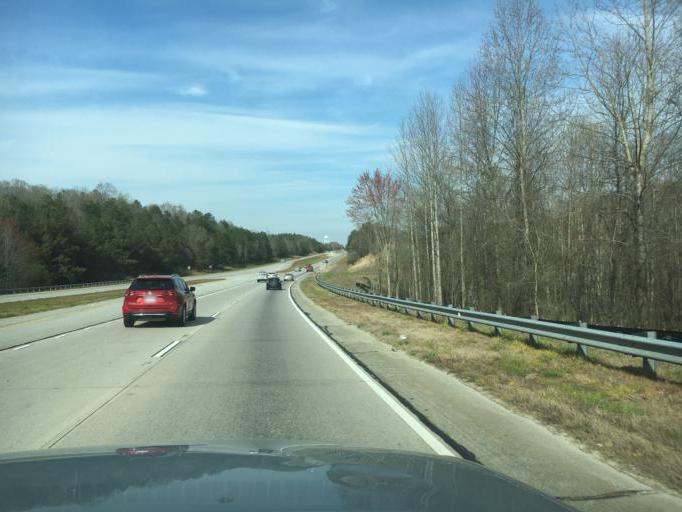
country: US
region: Georgia
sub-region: Hall County
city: Lula
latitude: 34.3851
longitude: -83.7076
